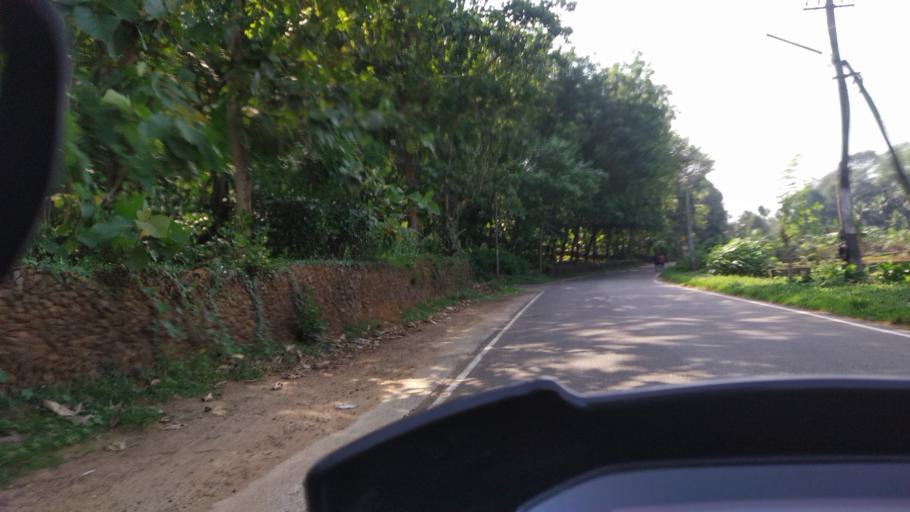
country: IN
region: Kerala
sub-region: Ernakulam
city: Piravam
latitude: 9.8128
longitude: 76.5656
